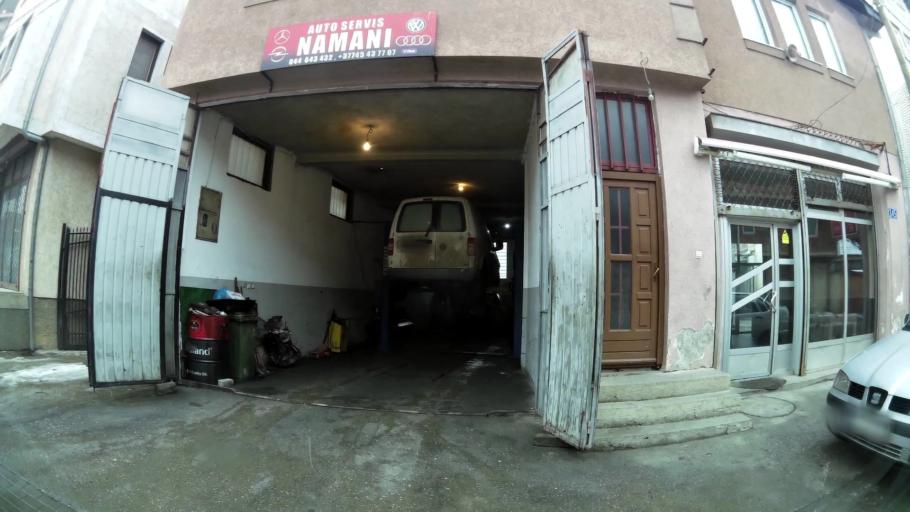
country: XK
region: Pristina
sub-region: Komuna e Prishtines
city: Pristina
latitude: 42.6743
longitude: 21.1727
